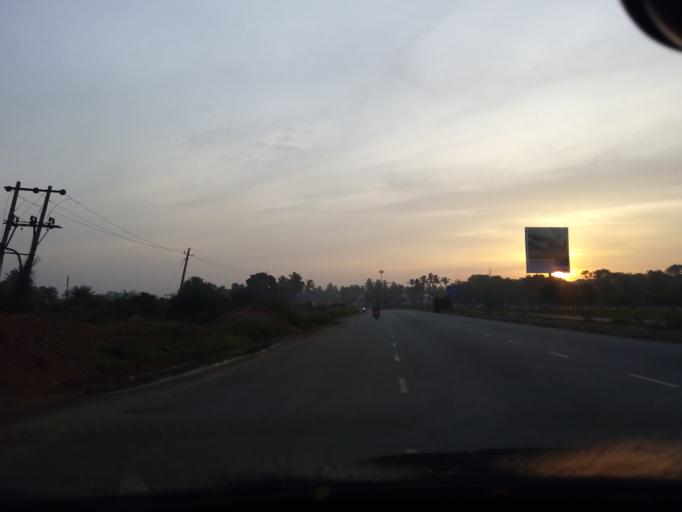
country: IN
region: Karnataka
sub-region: Bangalore Rural
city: Devanhalli
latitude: 13.2410
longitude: 77.7022
